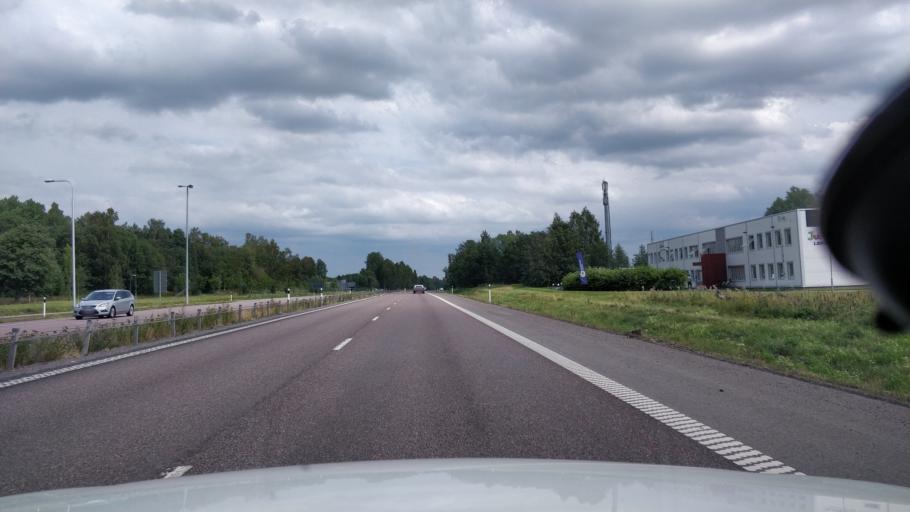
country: SE
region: Dalarna
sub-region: Borlange Kommun
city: Borlaenge
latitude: 60.4863
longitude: 15.4665
